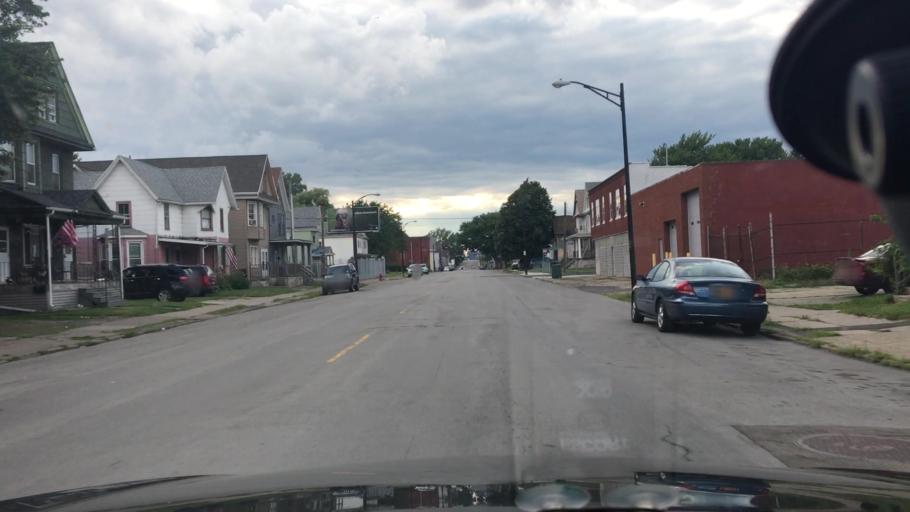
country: US
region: New York
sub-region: Erie County
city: West Seneca
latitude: 42.8690
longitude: -78.8304
